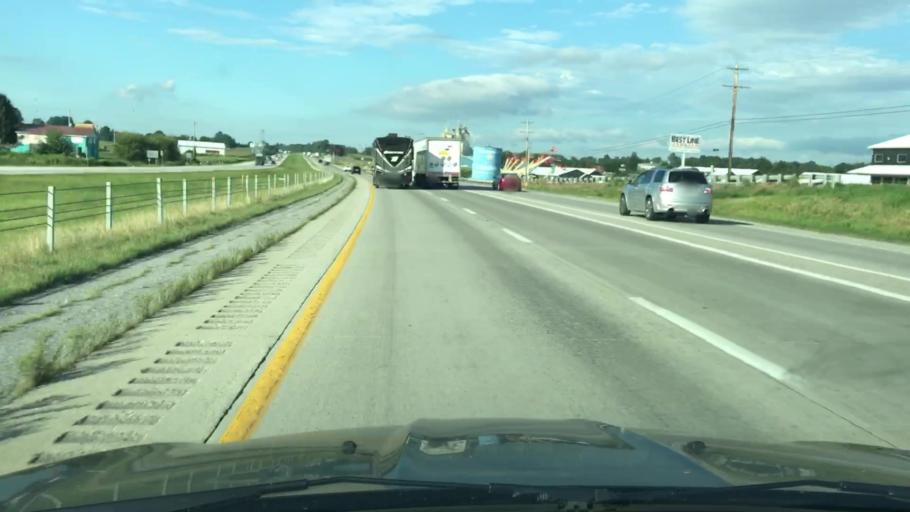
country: US
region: Pennsylvania
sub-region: Cumberland County
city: Shippensburg
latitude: 40.0142
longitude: -77.5362
